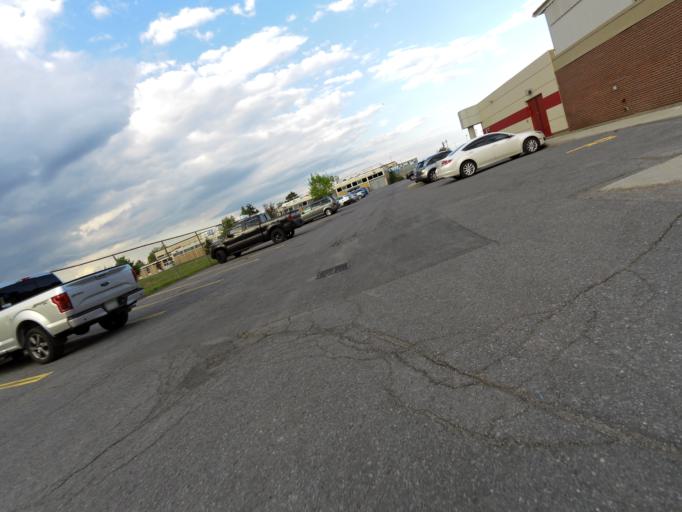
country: CA
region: Ontario
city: Bells Corners
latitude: 45.3249
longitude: -75.8111
